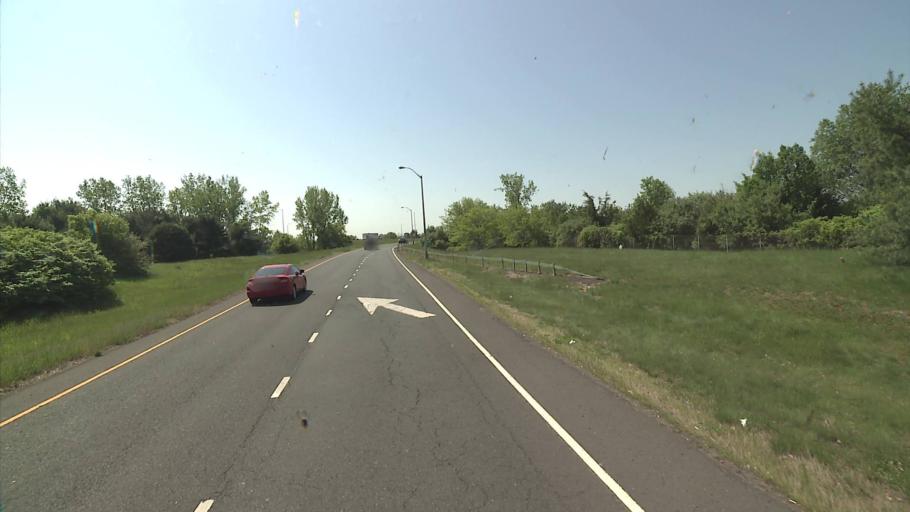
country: US
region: Connecticut
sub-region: Hartford County
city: Manchester
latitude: 41.8018
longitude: -72.5571
